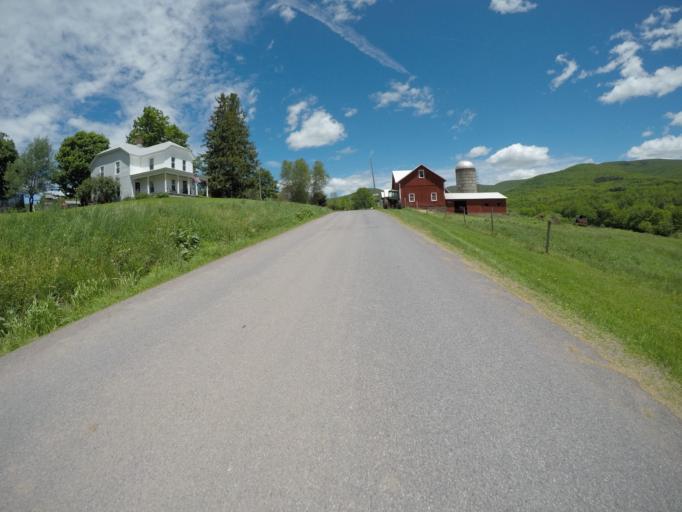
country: US
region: New York
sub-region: Delaware County
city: Stamford
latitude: 42.2639
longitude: -74.5202
